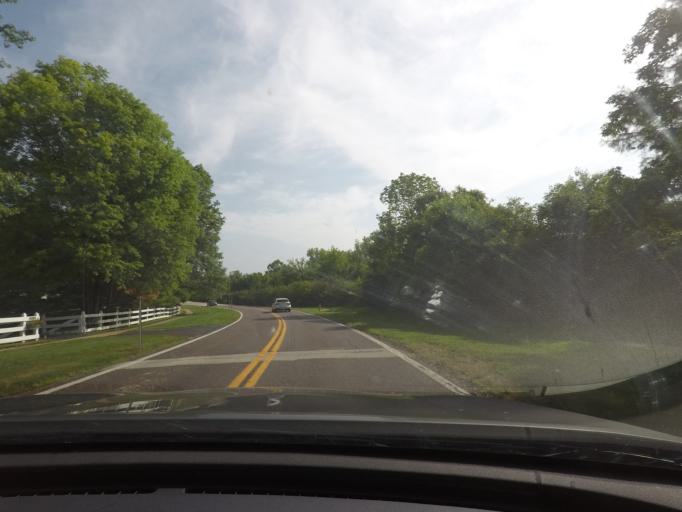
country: US
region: Missouri
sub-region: Saint Louis County
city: Town and Country
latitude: 38.6287
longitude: -90.4813
